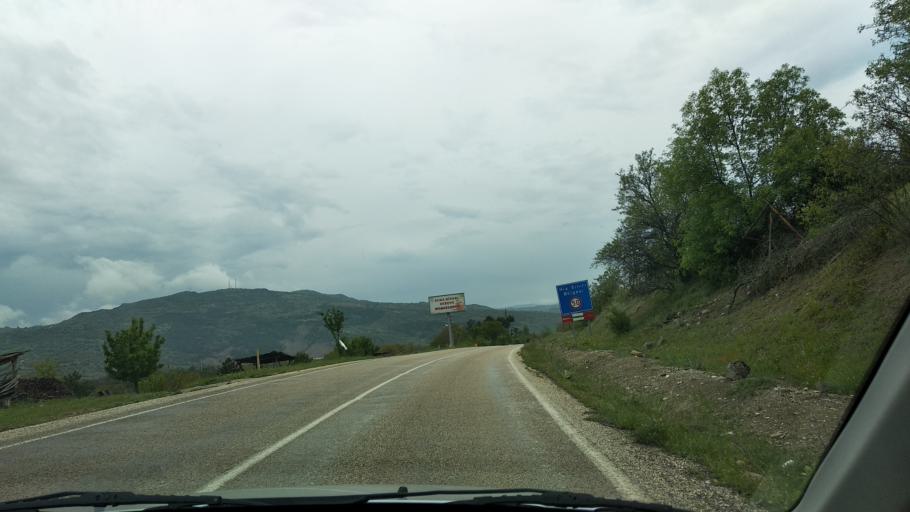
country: TR
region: Bolu
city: Seben
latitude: 40.4218
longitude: 31.5853
